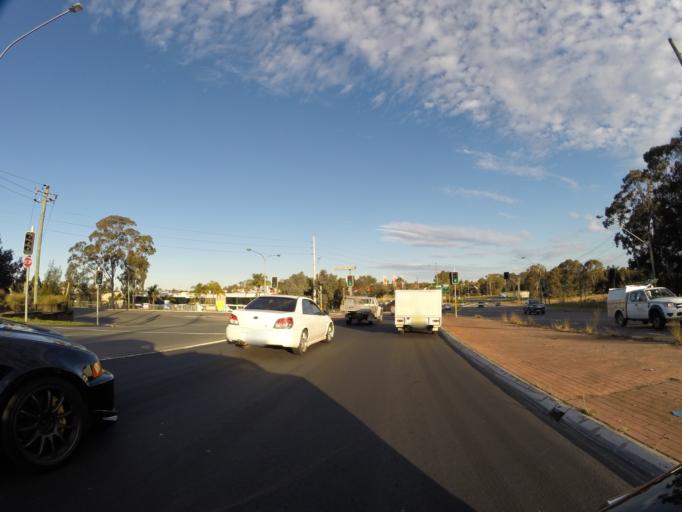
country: AU
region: New South Wales
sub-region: Fairfield
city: Horsley Park
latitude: -33.8490
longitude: 150.8765
